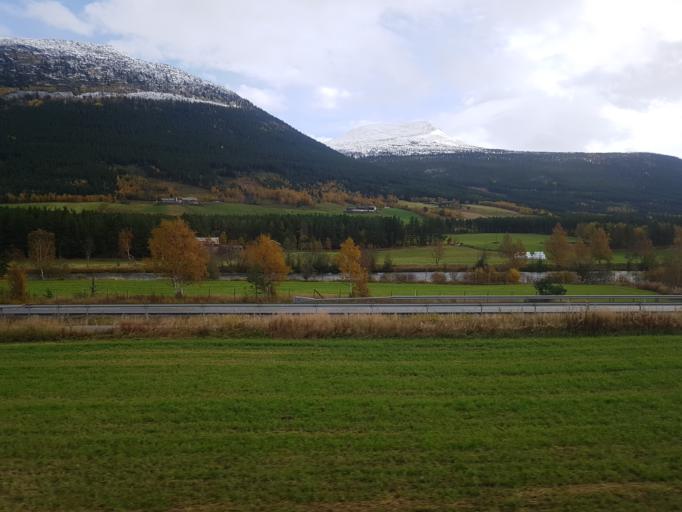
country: NO
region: Oppland
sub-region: Dovre
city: Dovre
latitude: 61.9290
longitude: 9.3209
